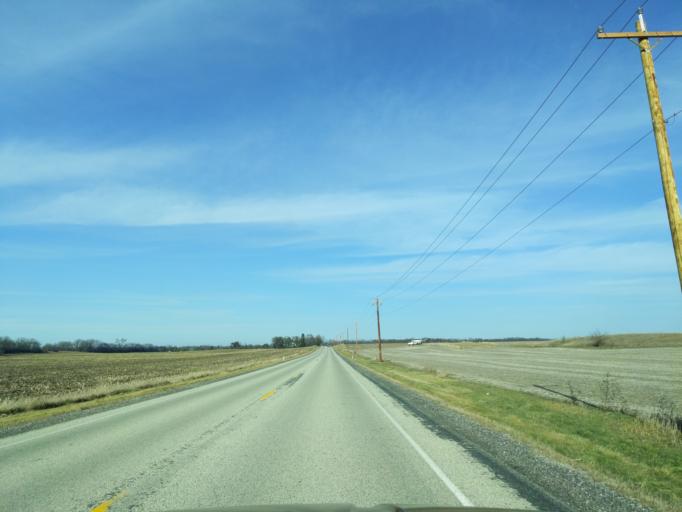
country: US
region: Wisconsin
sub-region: Walworth County
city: Elkhorn
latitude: 42.7393
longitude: -88.5922
